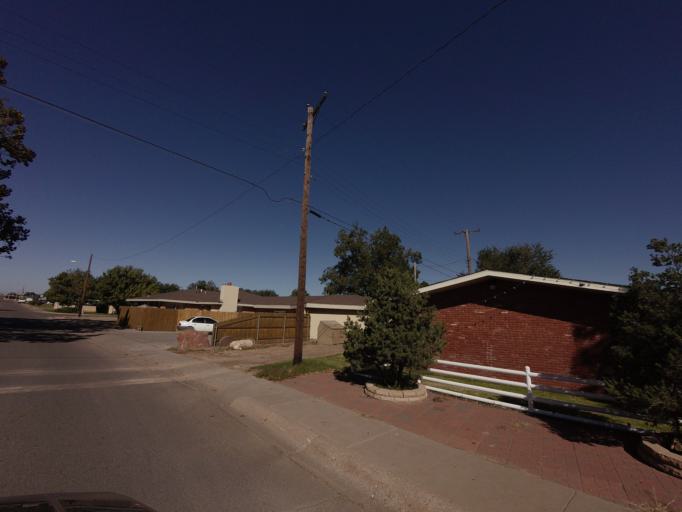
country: US
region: New Mexico
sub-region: Curry County
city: Clovis
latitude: 34.4278
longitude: -103.2020
